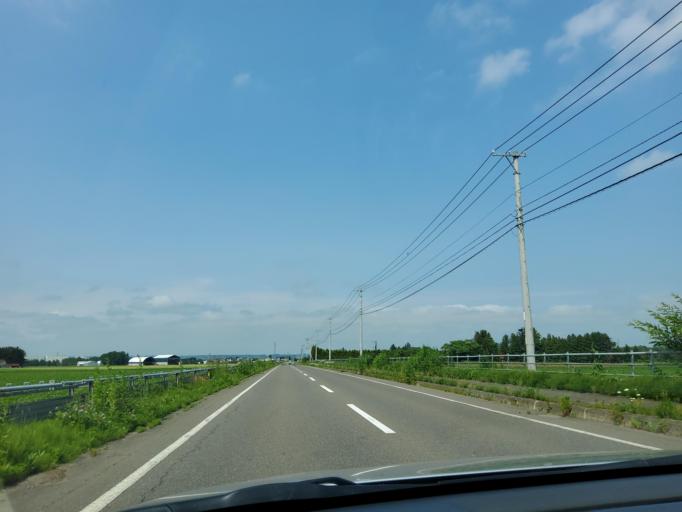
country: JP
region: Hokkaido
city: Obihiro
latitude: 42.8907
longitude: 143.0396
